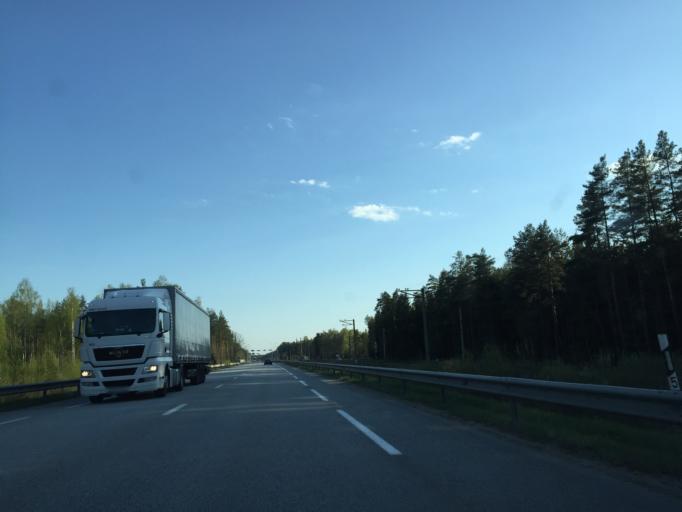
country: LV
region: Saulkrastu
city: Saulkrasti
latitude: 57.3111
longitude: 24.4452
